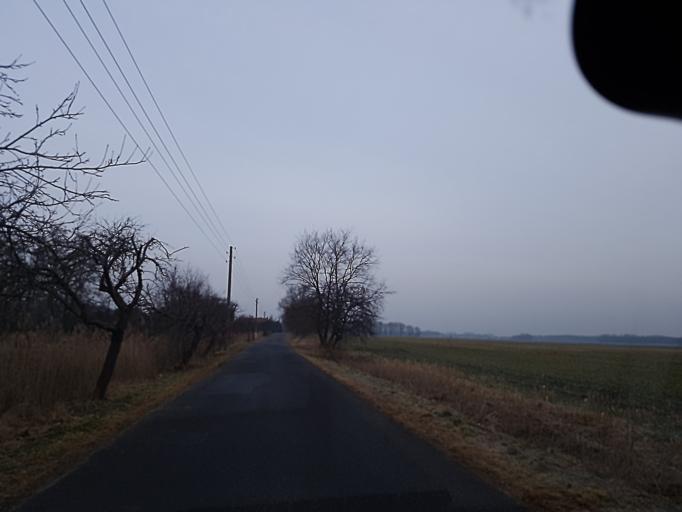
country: DE
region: Brandenburg
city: Ruckersdorf
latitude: 51.5708
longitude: 13.5438
